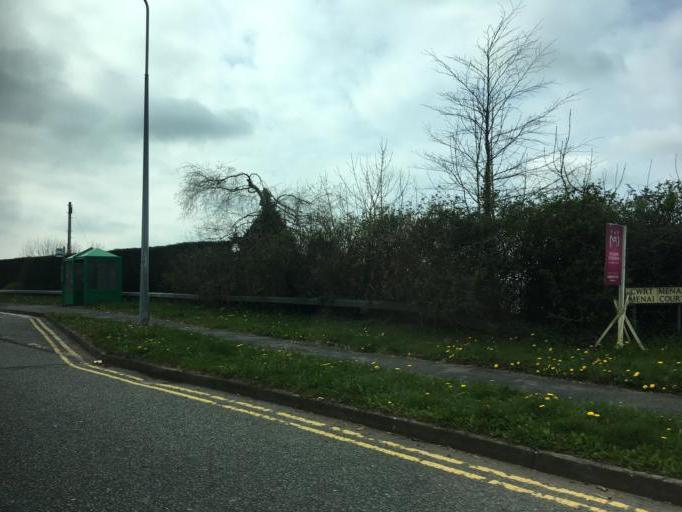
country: GB
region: Wales
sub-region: Gwynedd
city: Y Felinheli
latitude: 53.1826
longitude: -4.2107
